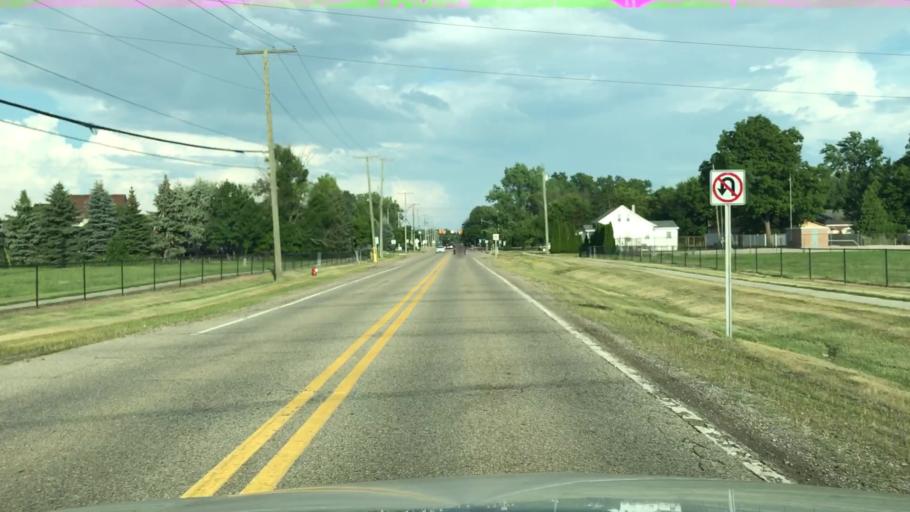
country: US
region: Michigan
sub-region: Macomb County
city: Sterling Heights
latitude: 42.5894
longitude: -82.9948
